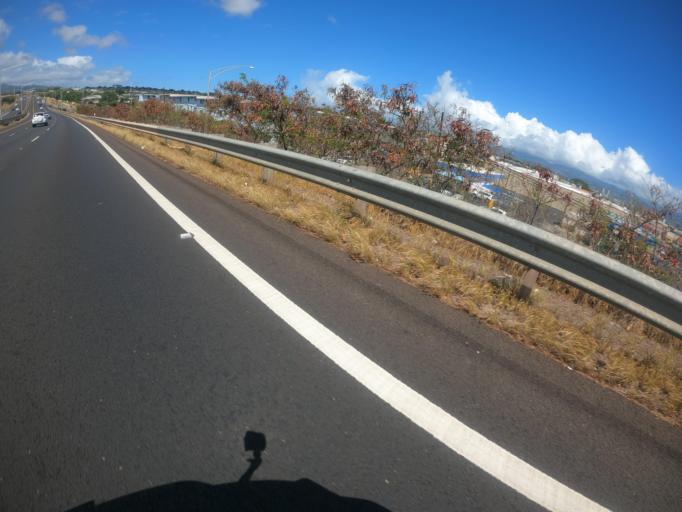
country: US
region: Hawaii
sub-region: Honolulu County
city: Royal Kunia
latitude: 21.3778
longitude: -158.0274
